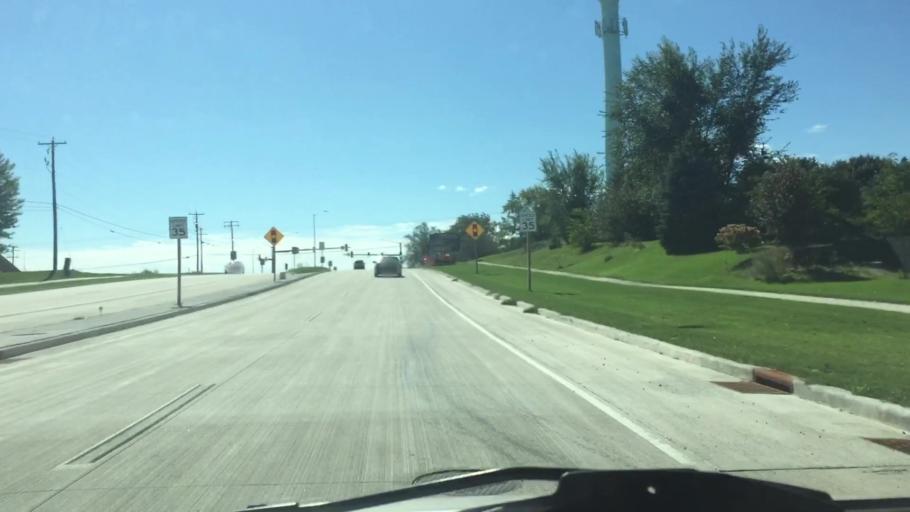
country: US
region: Wisconsin
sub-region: Waukesha County
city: Pewaukee
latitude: 43.0385
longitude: -88.2860
